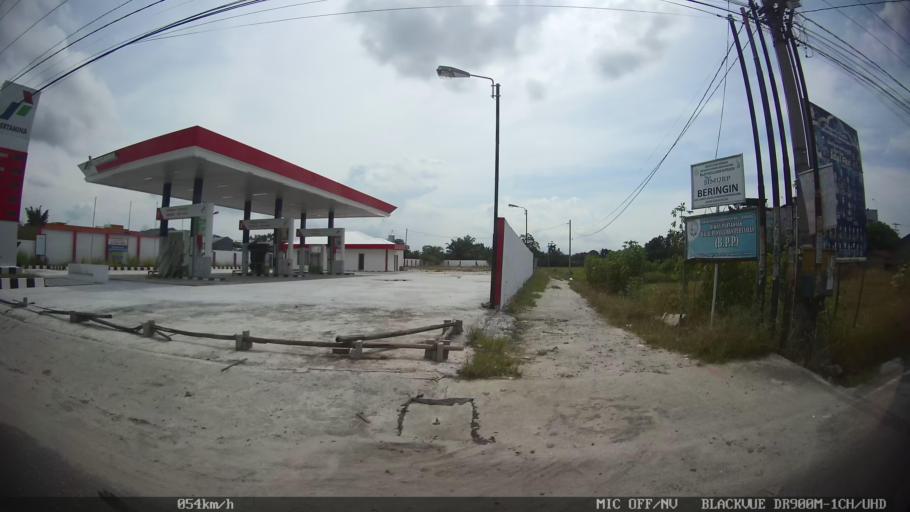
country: ID
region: North Sumatra
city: Percut
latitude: 3.5914
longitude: 98.8587
